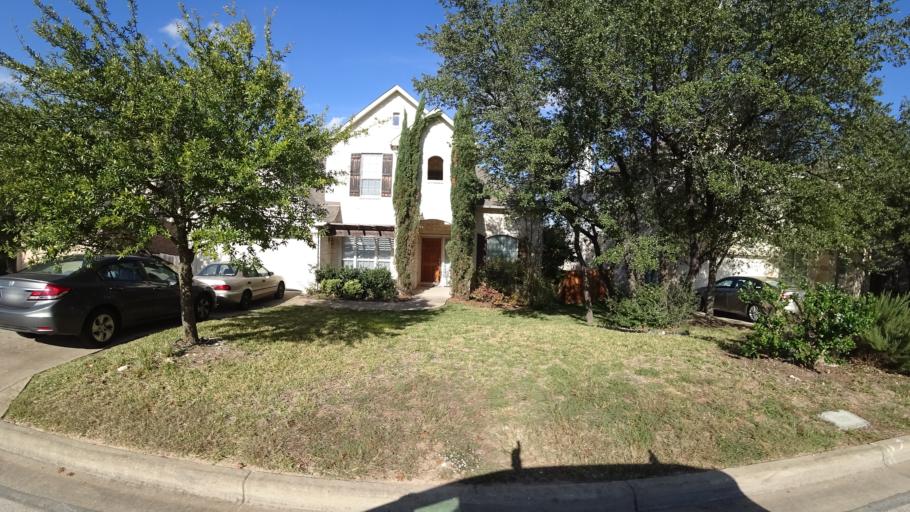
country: US
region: Texas
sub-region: Travis County
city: Barton Creek
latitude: 30.2510
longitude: -97.8747
